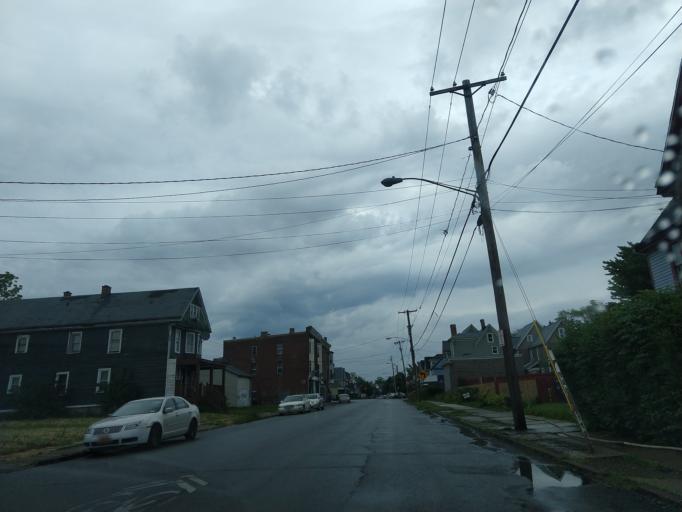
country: US
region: New York
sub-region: Erie County
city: Buffalo
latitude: 42.9132
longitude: -78.8914
